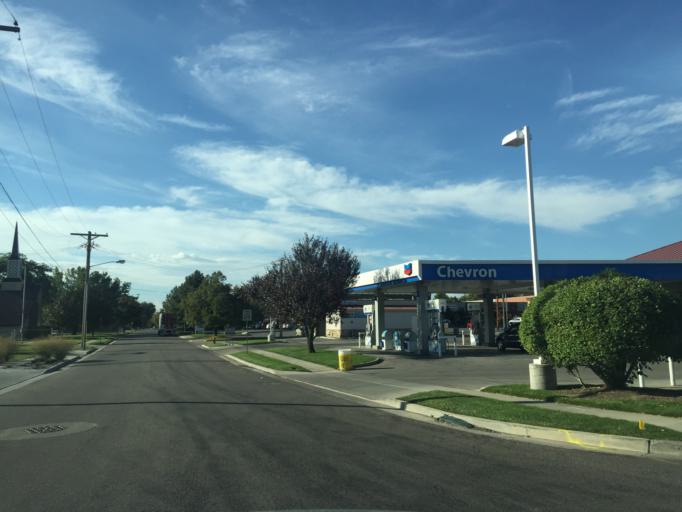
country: US
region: Utah
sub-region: Salt Lake County
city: Murray
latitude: 40.6540
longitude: -111.9076
